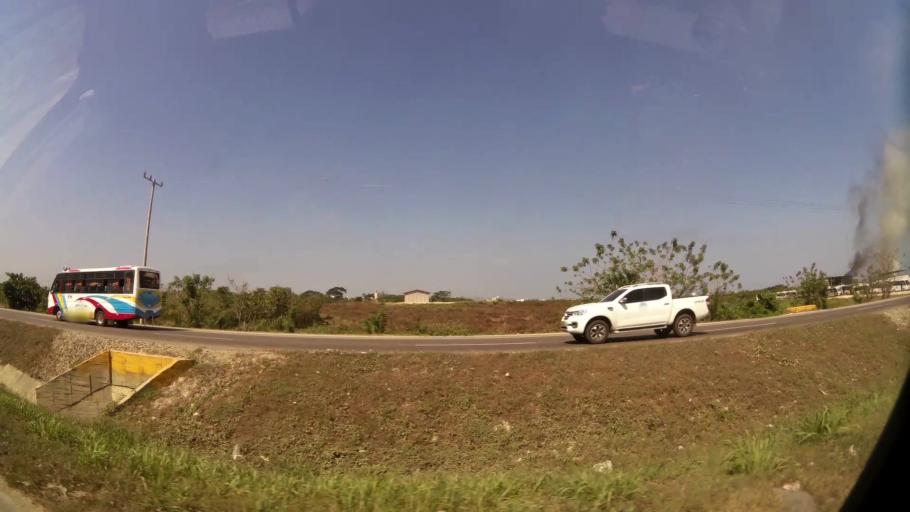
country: CO
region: Bolivar
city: Cartagena
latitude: 10.3973
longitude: -75.4469
